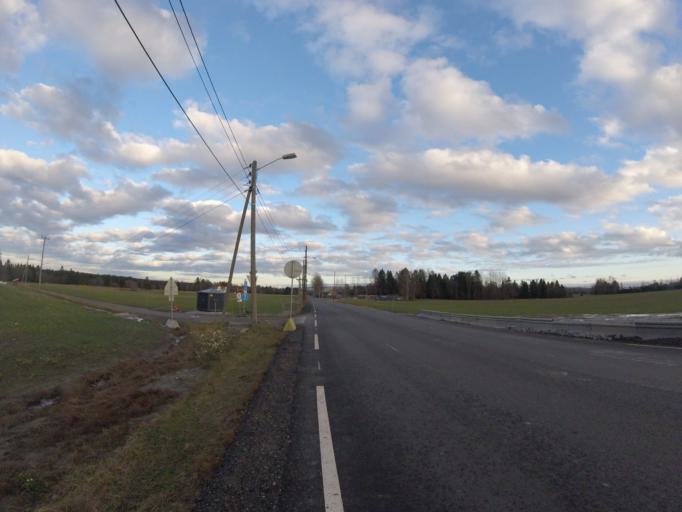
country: NO
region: Akershus
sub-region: Skedsmo
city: Leirsund
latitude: 59.9982
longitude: 11.0474
